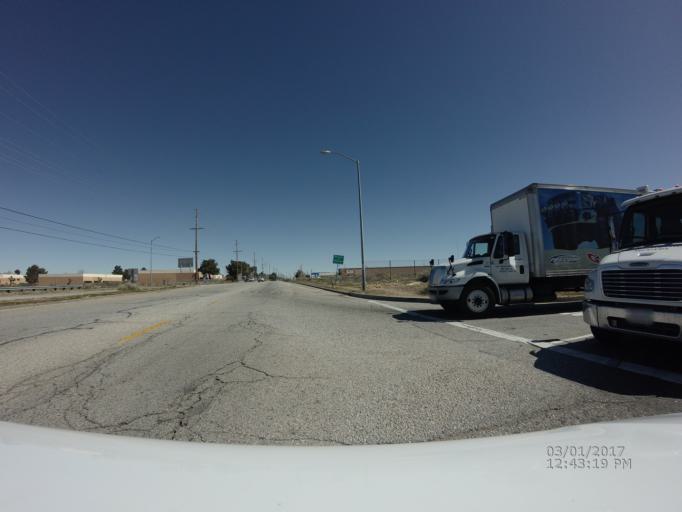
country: US
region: California
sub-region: Los Angeles County
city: Lancaster
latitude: 34.6457
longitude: -118.1518
